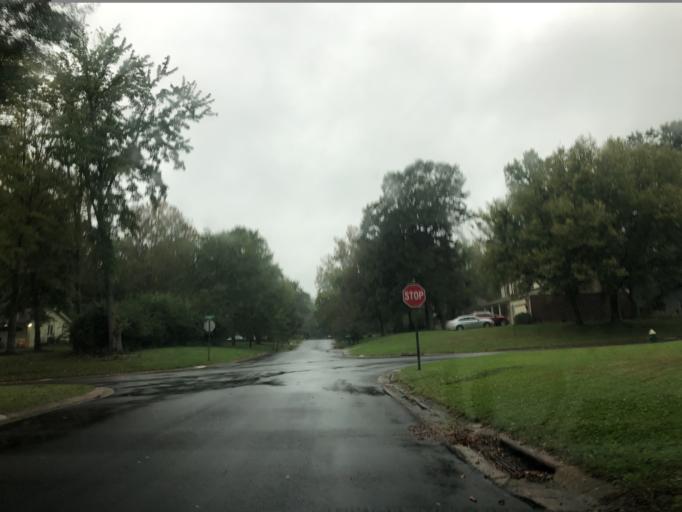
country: US
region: Ohio
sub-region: Hamilton County
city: The Village of Indian Hill
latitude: 39.2665
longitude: -84.2880
